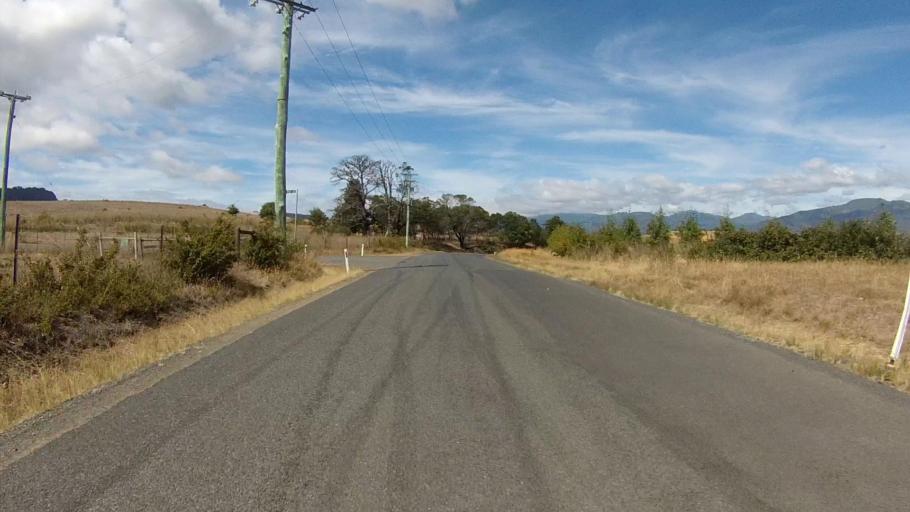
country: AU
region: Tasmania
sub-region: Brighton
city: Old Beach
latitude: -42.7430
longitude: 147.3027
